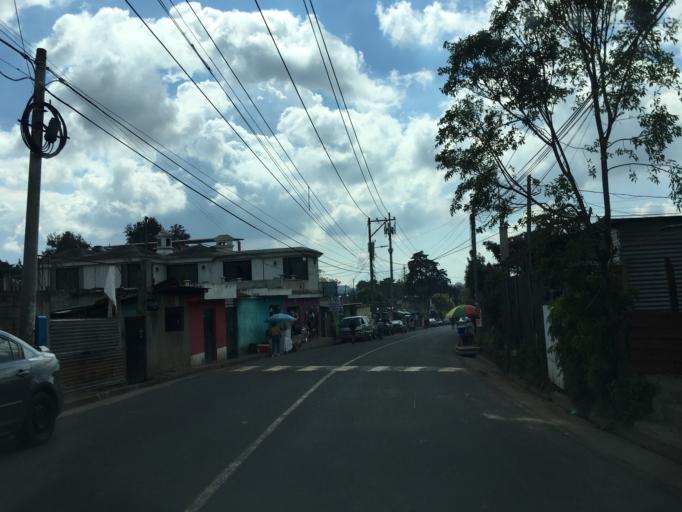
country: GT
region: Guatemala
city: San Jose Pinula
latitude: 14.5555
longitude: -90.4444
